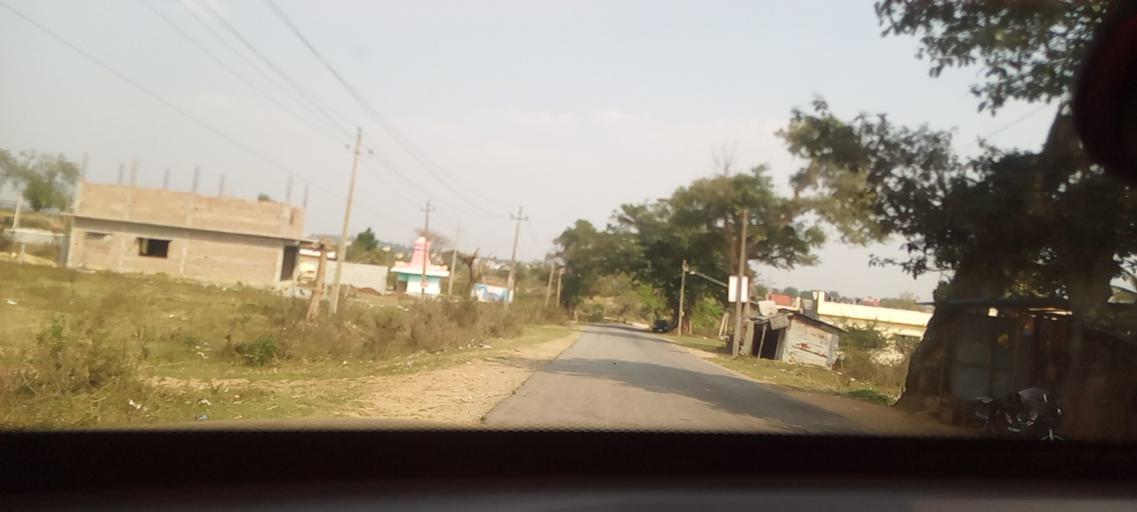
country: IN
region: Karnataka
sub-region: Hassan
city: Belur
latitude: 13.1734
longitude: 75.8580
